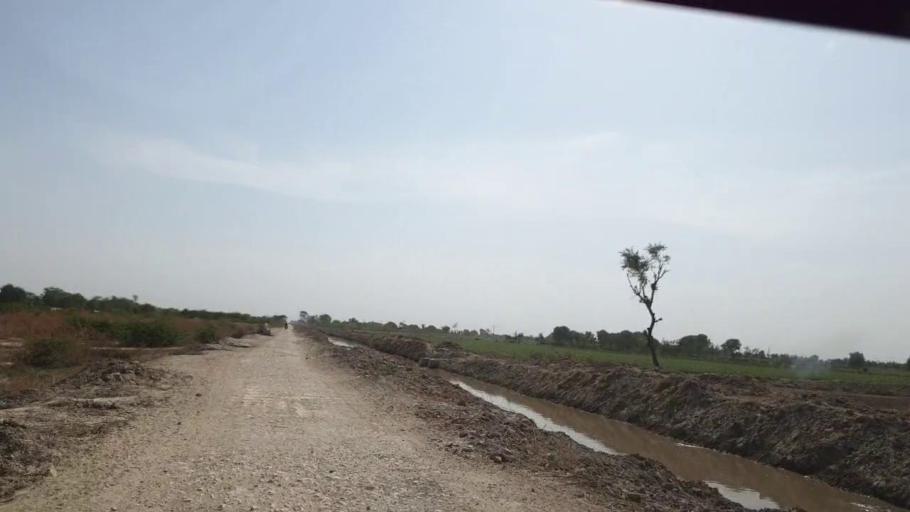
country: PK
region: Sindh
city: Nabisar
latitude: 25.0819
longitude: 69.5801
